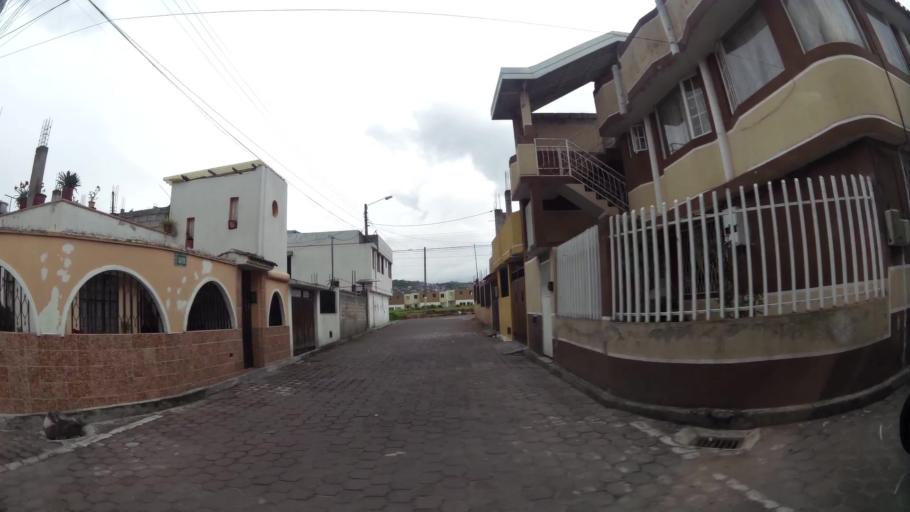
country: EC
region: Pichincha
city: Quito
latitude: -0.3149
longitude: -78.5470
